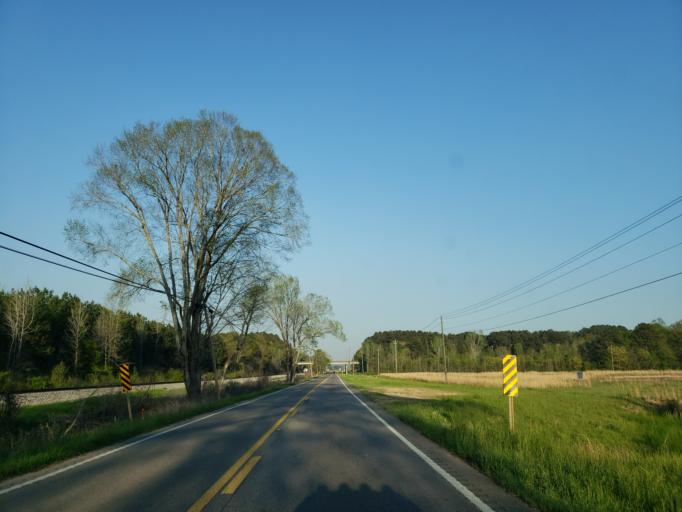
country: US
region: Mississippi
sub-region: Lauderdale County
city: Marion
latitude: 32.3941
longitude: -88.6442
